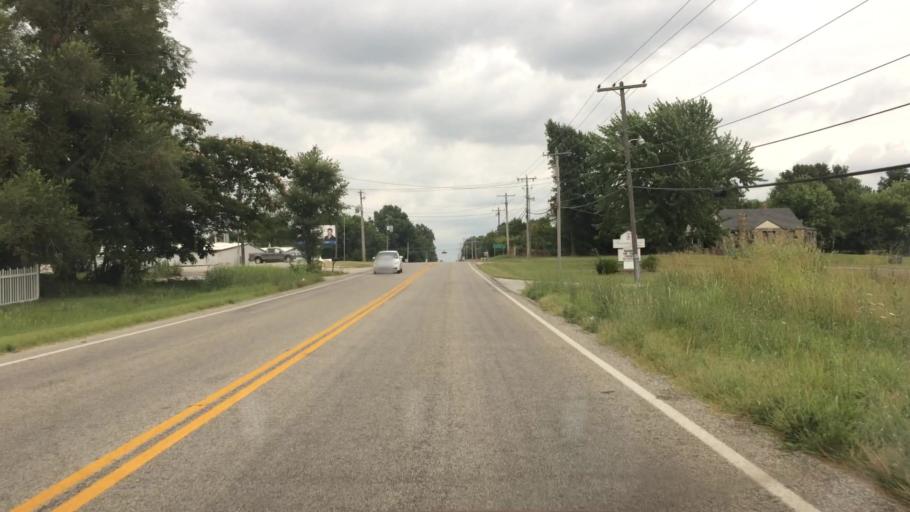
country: US
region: Missouri
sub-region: Greene County
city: Springfield
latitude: 37.2932
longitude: -93.2638
